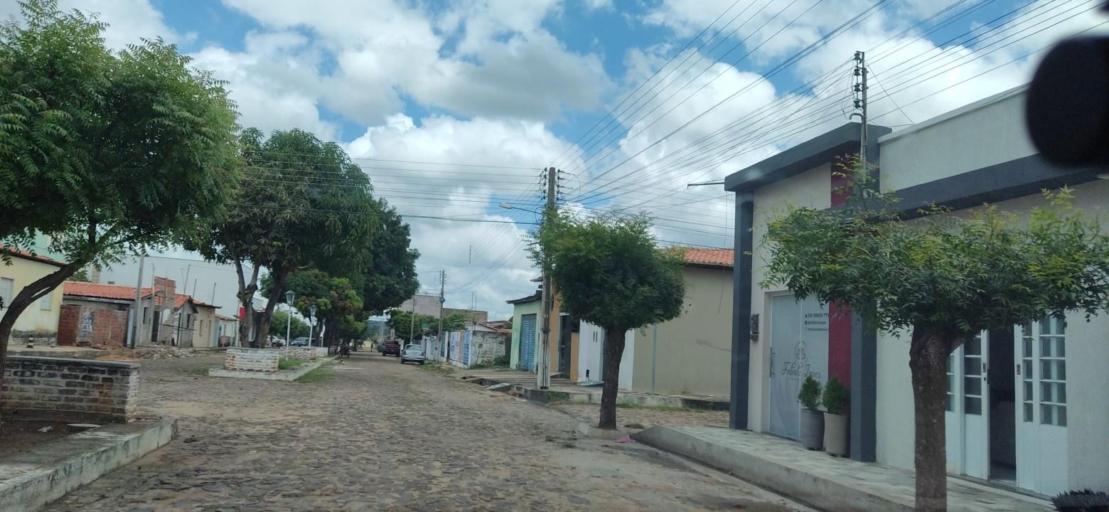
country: BR
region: Piaui
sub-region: Valenca Do Piaui
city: Valenca do Piaui
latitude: -6.4011
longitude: -41.7362
